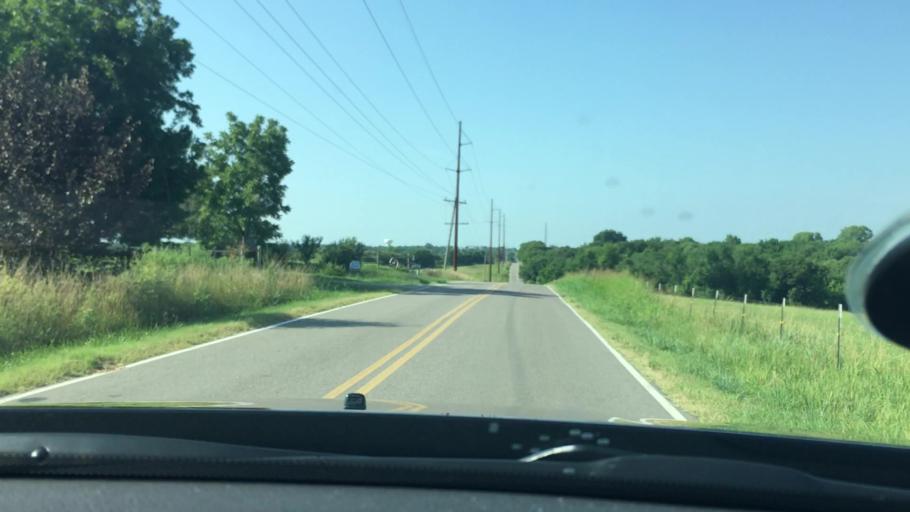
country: US
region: Oklahoma
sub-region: Pontotoc County
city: Ada
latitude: 34.8014
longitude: -96.6348
